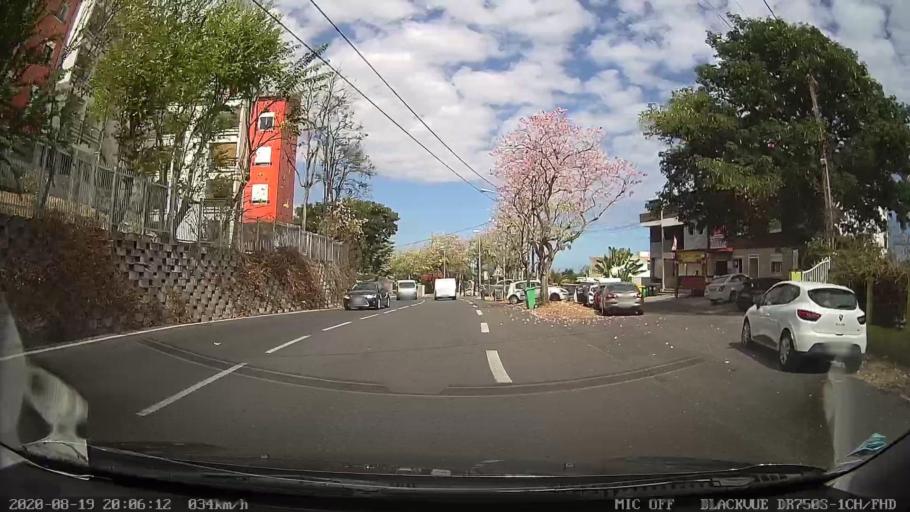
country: RE
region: Reunion
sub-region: Reunion
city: La Possession
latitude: -20.9564
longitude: 55.3369
